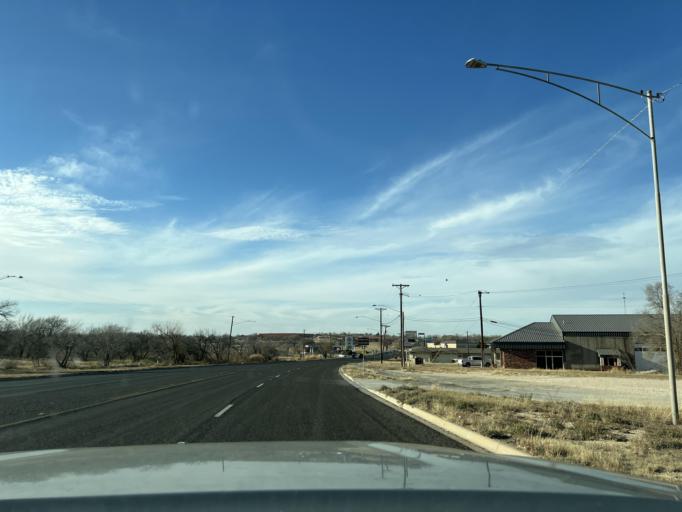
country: US
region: Texas
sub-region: Scurry County
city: Snyder
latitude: 32.7029
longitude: -100.8809
